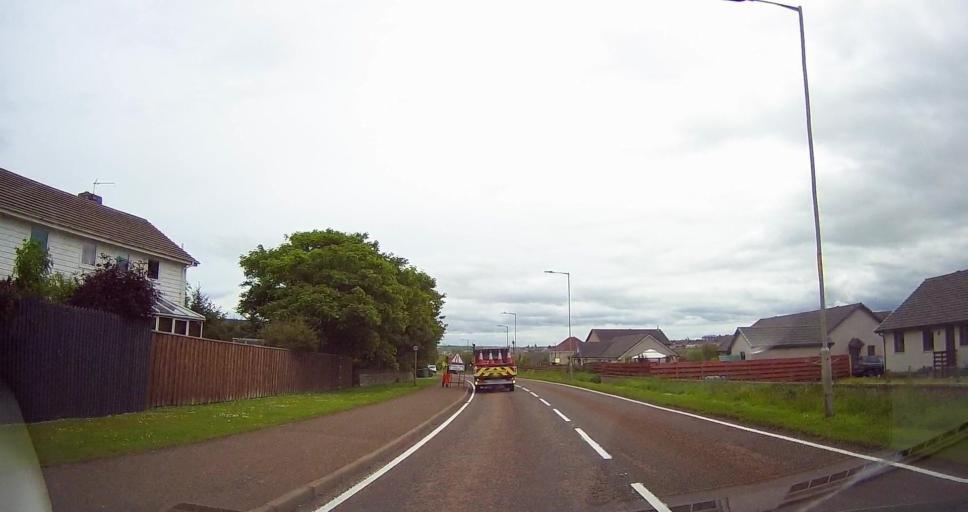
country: GB
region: Scotland
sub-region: Highland
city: Thurso
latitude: 58.6028
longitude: -3.5481
